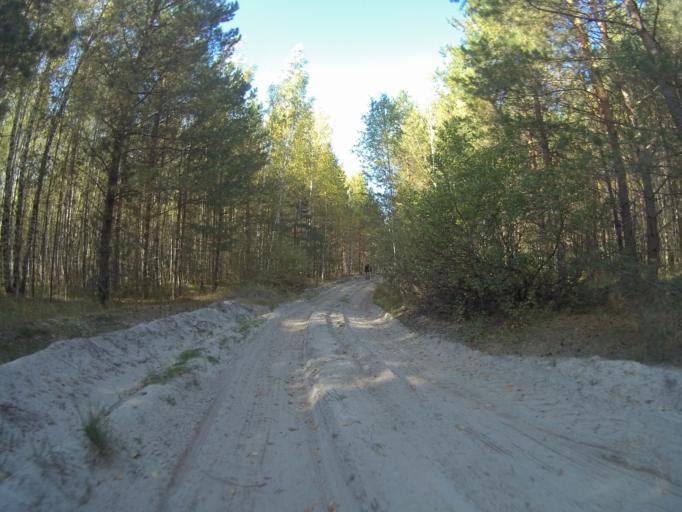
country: RU
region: Vladimir
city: Vorsha
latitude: 55.9037
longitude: 40.1725
